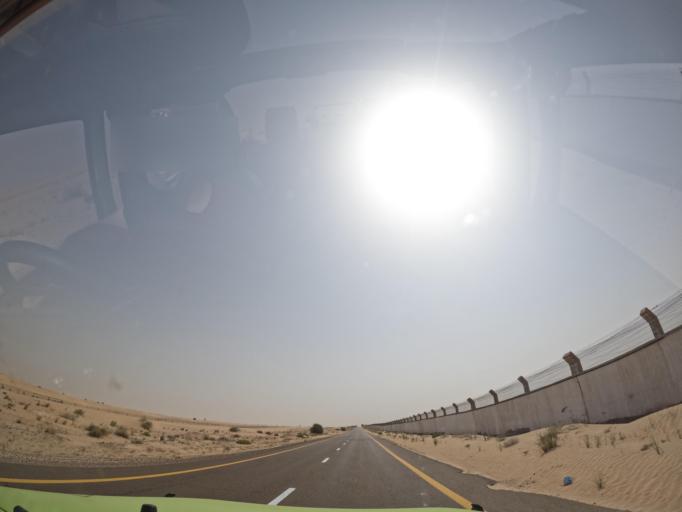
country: AE
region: Dubai
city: Dubai
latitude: 24.6196
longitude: 55.3539
